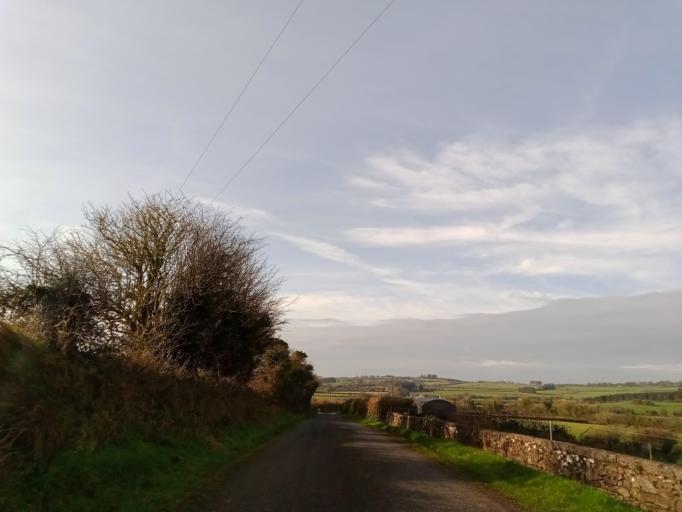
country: IE
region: Munster
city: Fethard
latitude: 52.5627
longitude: -7.6167
